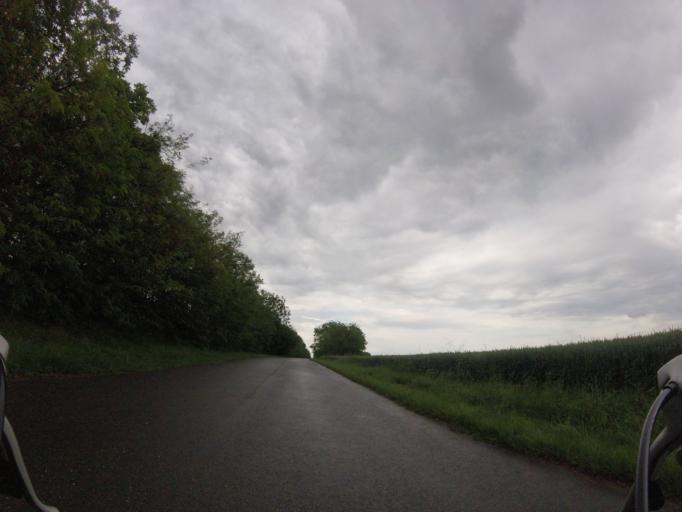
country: HU
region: Baranya
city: Pellerd
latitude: 45.9650
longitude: 18.1949
